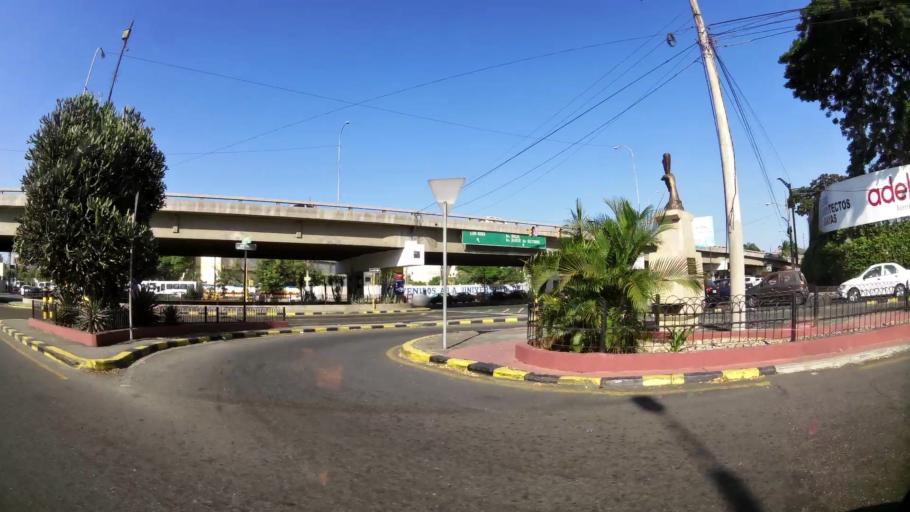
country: EC
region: Guayas
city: Guayaquil
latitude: -2.1796
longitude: -79.8969
